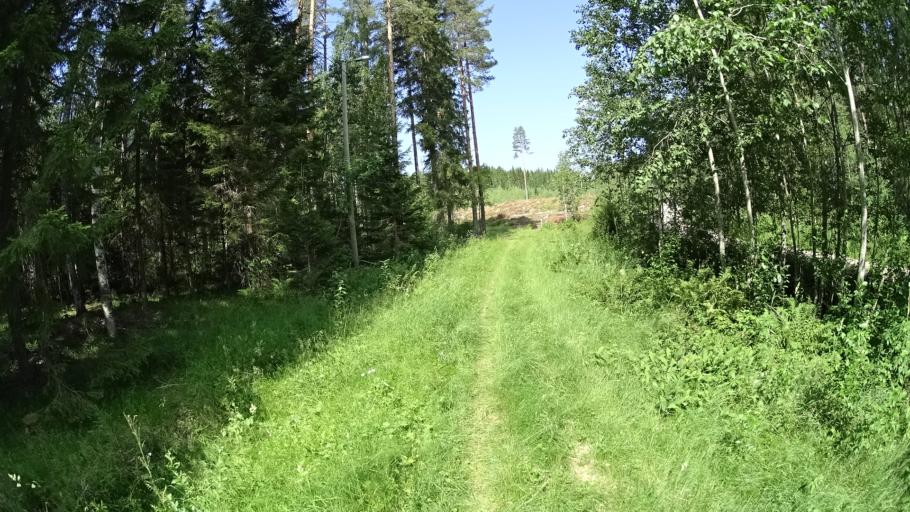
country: FI
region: North Karelia
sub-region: Pielisen Karjala
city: Lieksa
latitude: 63.1239
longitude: 29.8047
